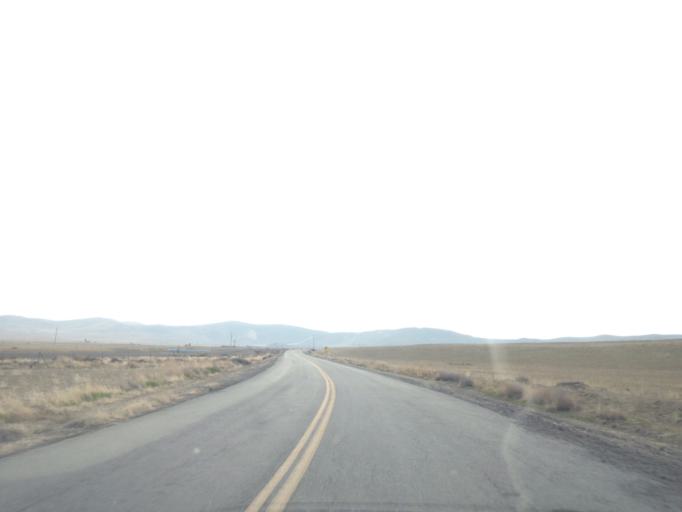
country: US
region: California
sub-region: Kings County
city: Kettleman City
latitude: 35.7275
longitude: -119.9935
